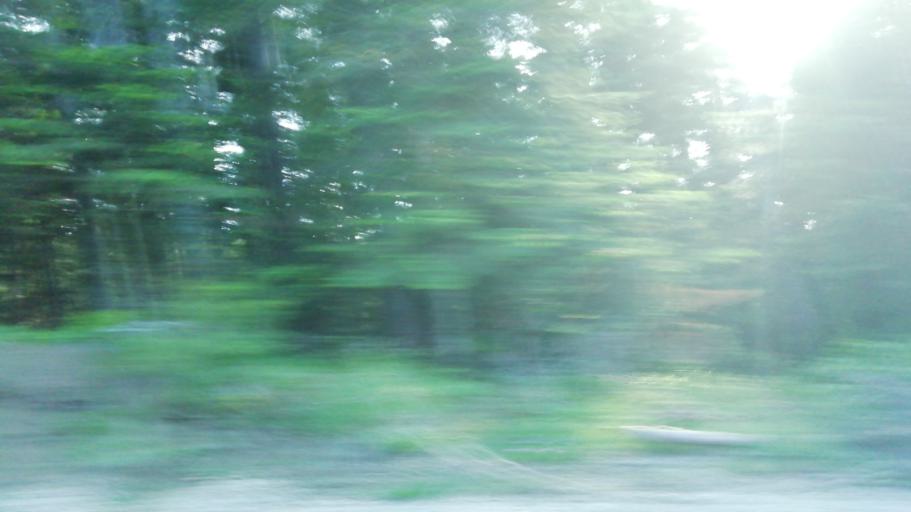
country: TR
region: Karabuk
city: Eskipazar
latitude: 41.0497
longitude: 32.5430
